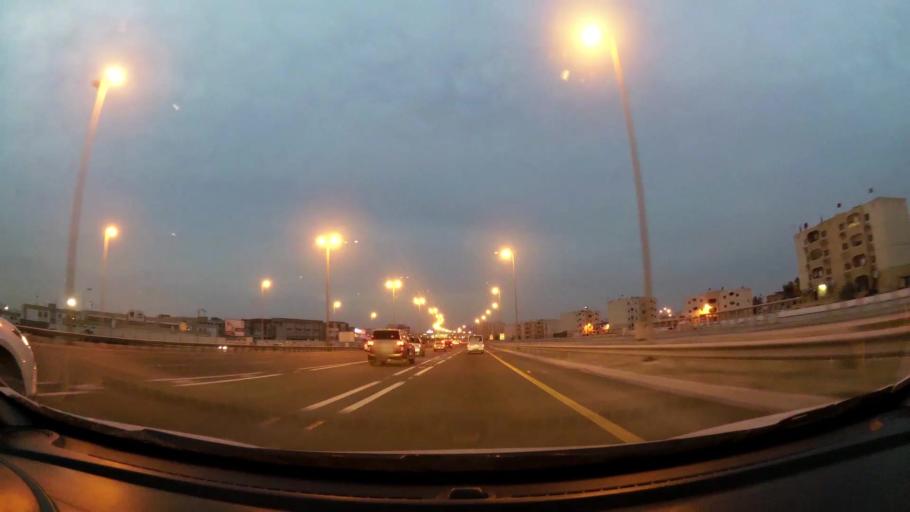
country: BH
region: Northern
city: Madinat `Isa
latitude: 26.1761
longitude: 50.5407
